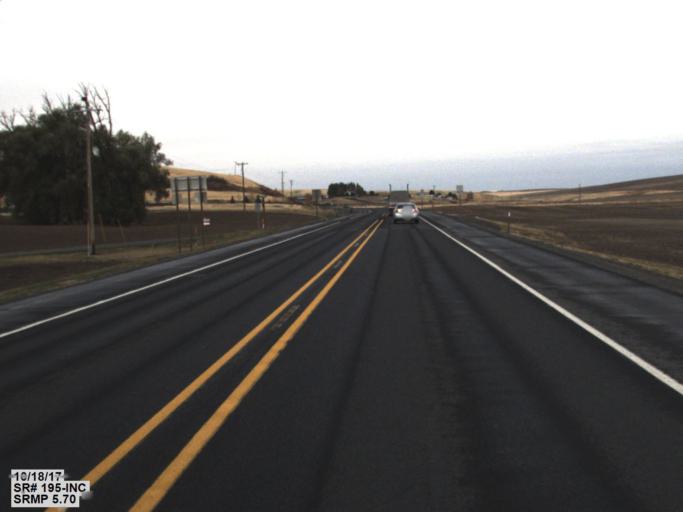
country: US
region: Washington
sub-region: Asotin County
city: Clarkston
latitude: 46.5454
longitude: -117.0919
